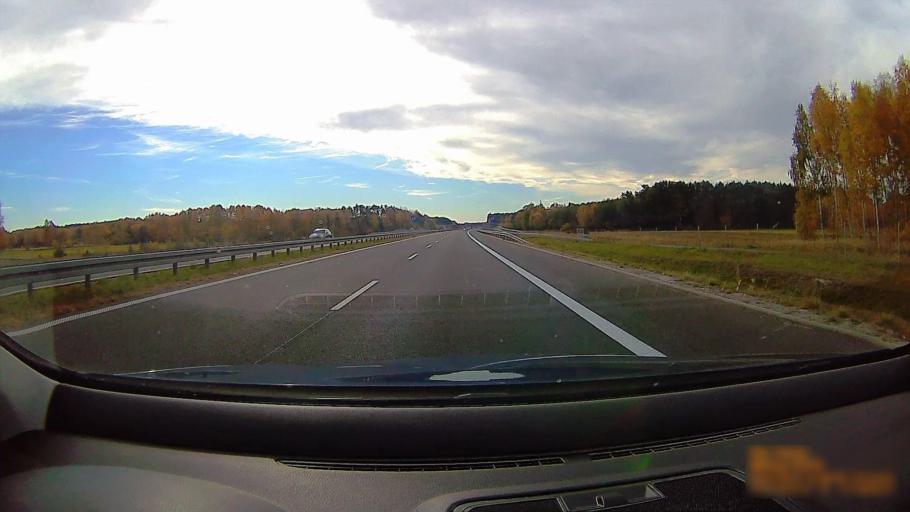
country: PL
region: Greater Poland Voivodeship
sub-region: Powiat ostrowski
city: Przygodzice
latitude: 51.5722
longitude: 17.8486
